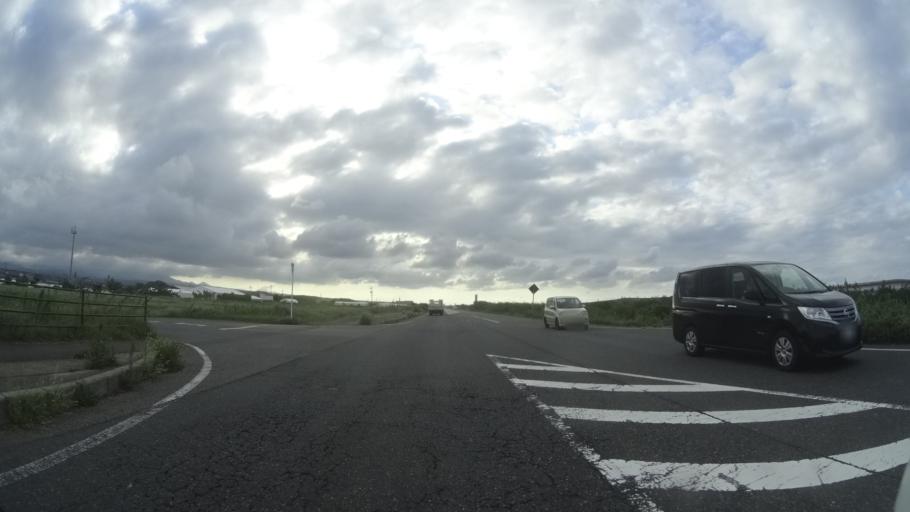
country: JP
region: Tottori
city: Kurayoshi
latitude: 35.5008
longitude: 133.7388
